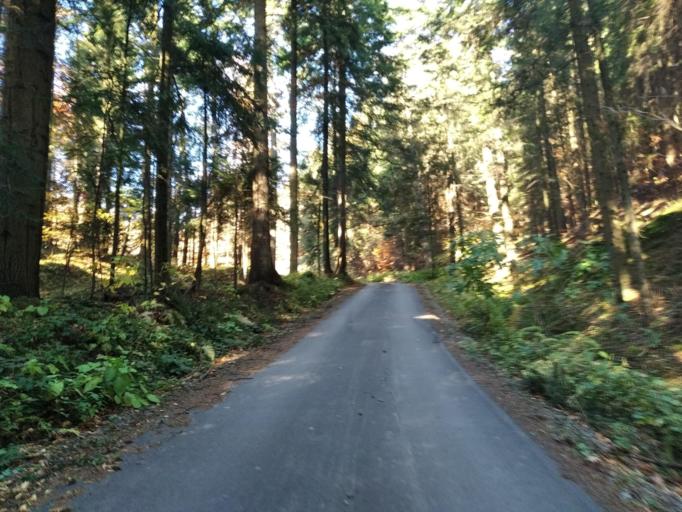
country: PL
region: Subcarpathian Voivodeship
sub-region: Powiat strzyzowski
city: Frysztak
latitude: 49.8538
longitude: 21.6106
